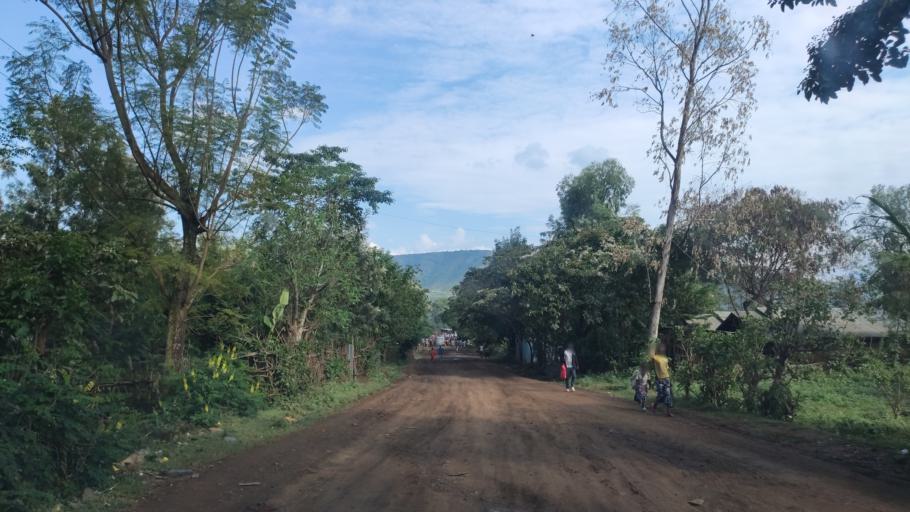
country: ET
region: Southern Nations, Nationalities, and People's Region
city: Felege Neway
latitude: 6.4260
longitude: 37.3072
